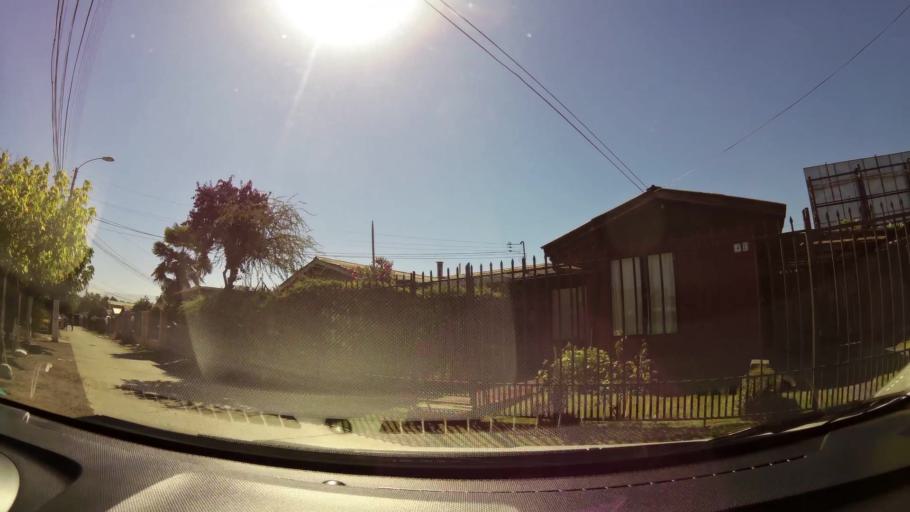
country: CL
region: O'Higgins
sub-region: Provincia de Cachapoal
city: Rancagua
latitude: -34.1749
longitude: -70.7046
